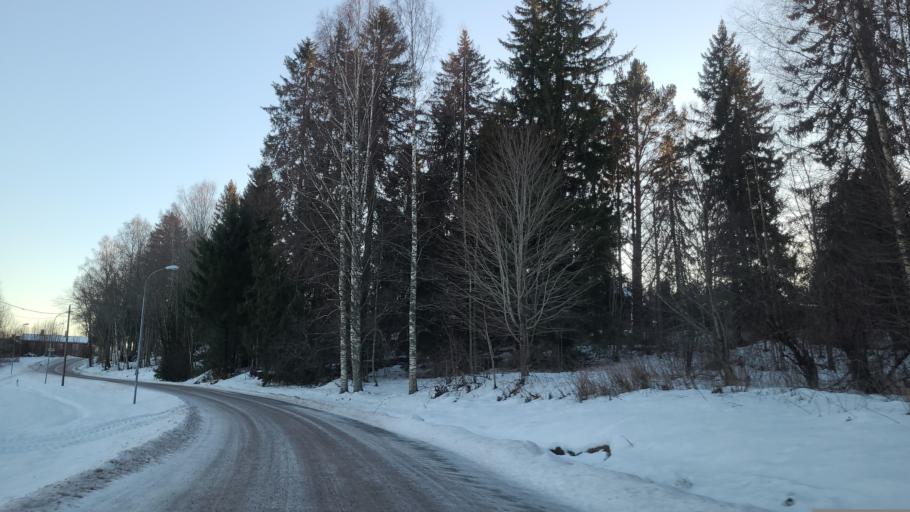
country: SE
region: Gaevleborg
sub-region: Soderhamns Kommun
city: Soderhamn
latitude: 61.2757
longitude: 16.9894
